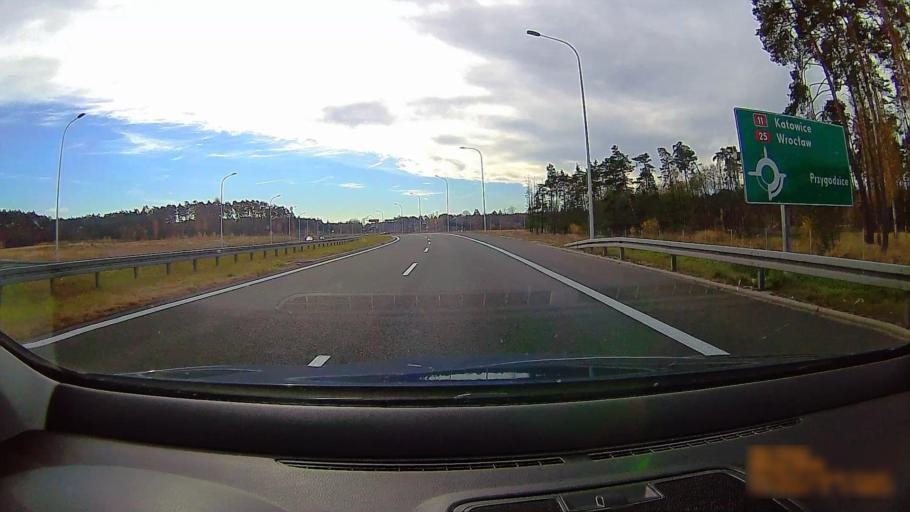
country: PL
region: Greater Poland Voivodeship
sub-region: Powiat ostrowski
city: Przygodzice
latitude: 51.5606
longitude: 17.8460
